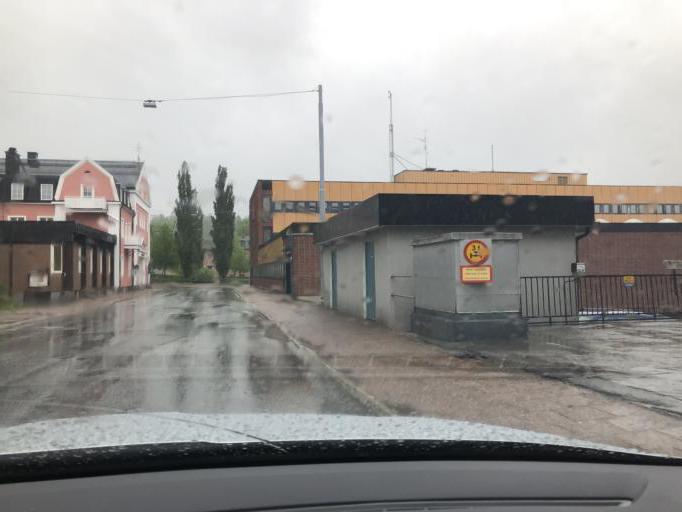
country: SE
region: Vaesternorrland
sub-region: OErnskoeldsviks Kommun
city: Ornskoldsvik
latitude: 63.2921
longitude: 18.7173
